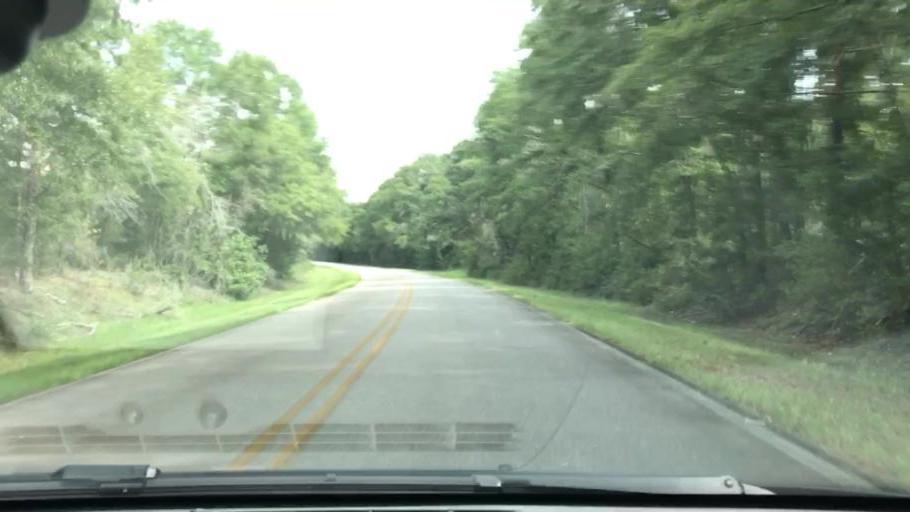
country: US
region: Georgia
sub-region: Clay County
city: Fort Gaines
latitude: 31.5729
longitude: -85.0152
